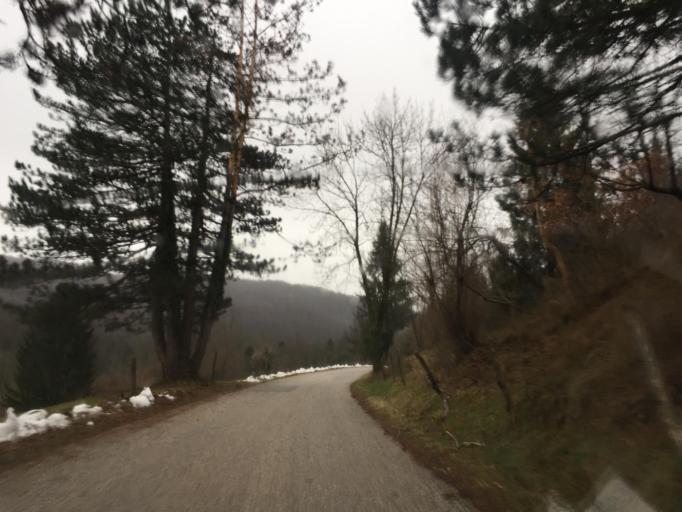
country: SI
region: Kanal
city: Kanal
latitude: 46.0737
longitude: 13.6649
